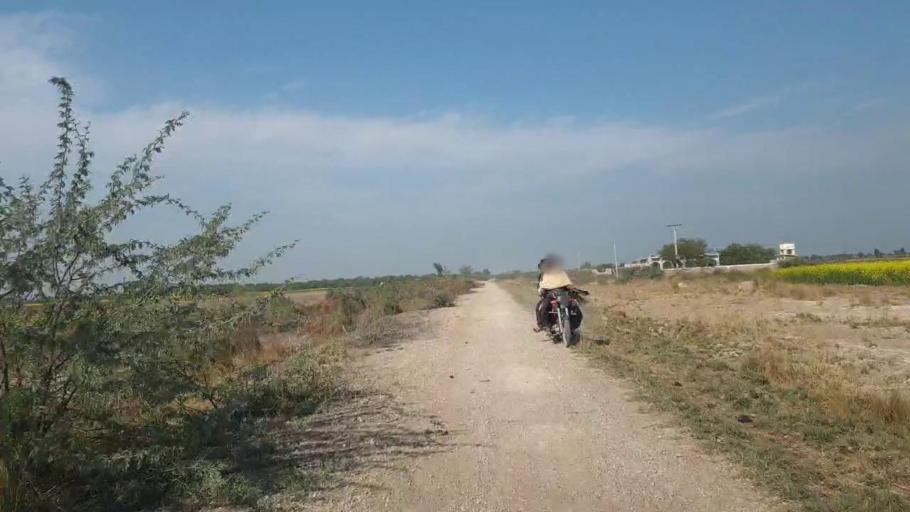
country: PK
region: Sindh
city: Shahdadpur
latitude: 25.9896
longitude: 68.5476
